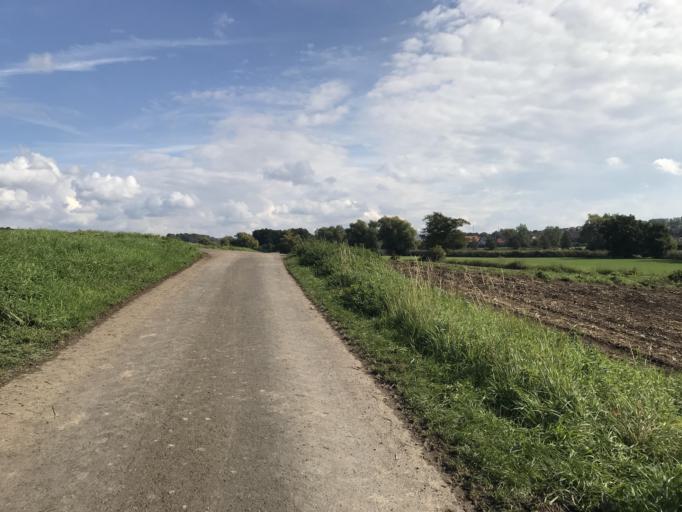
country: DE
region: Hesse
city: Gudensberg
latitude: 51.1550
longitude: 9.3725
